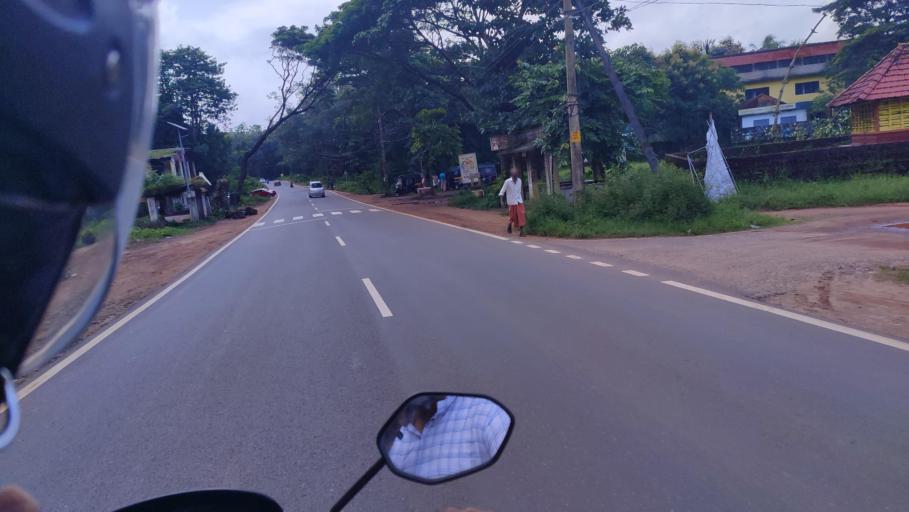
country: IN
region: Kerala
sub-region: Kasaragod District
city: Nileshwar
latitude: 12.2254
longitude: 75.1582
